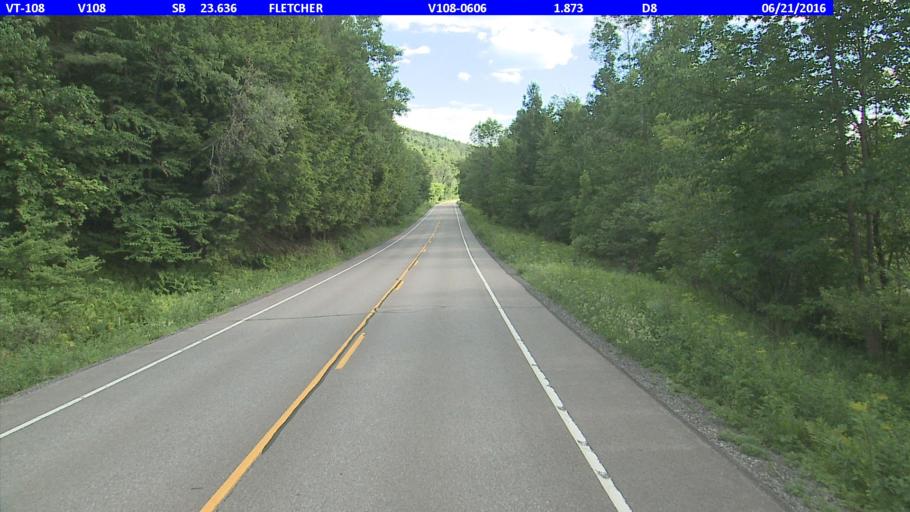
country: US
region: Vermont
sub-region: Lamoille County
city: Johnson
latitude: 44.7272
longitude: -72.8297
